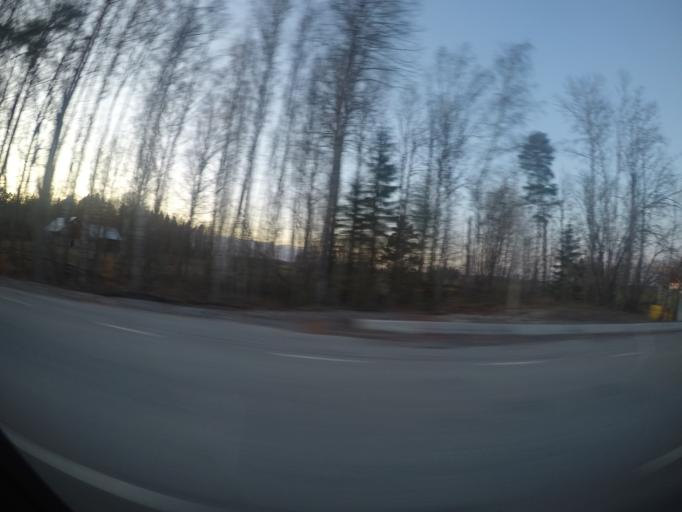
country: SE
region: OErebro
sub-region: Lindesbergs Kommun
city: Frovi
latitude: 59.3169
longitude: 15.3858
